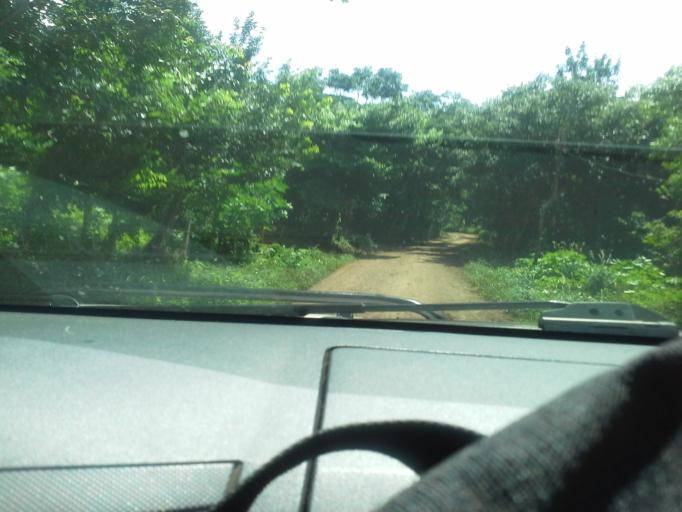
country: NI
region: Matagalpa
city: Terrabona
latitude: 12.7359
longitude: -85.9272
